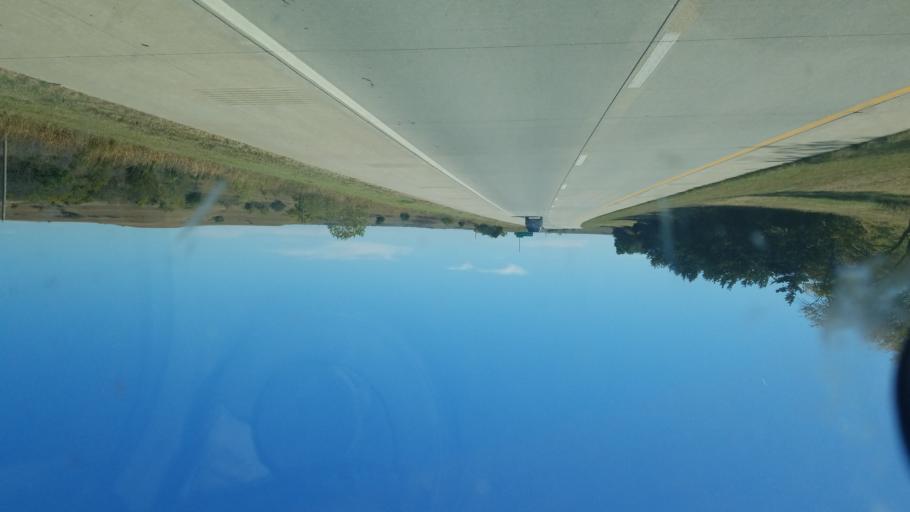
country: US
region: Kansas
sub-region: Riley County
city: Ogden
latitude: 39.0675
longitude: -96.6309
